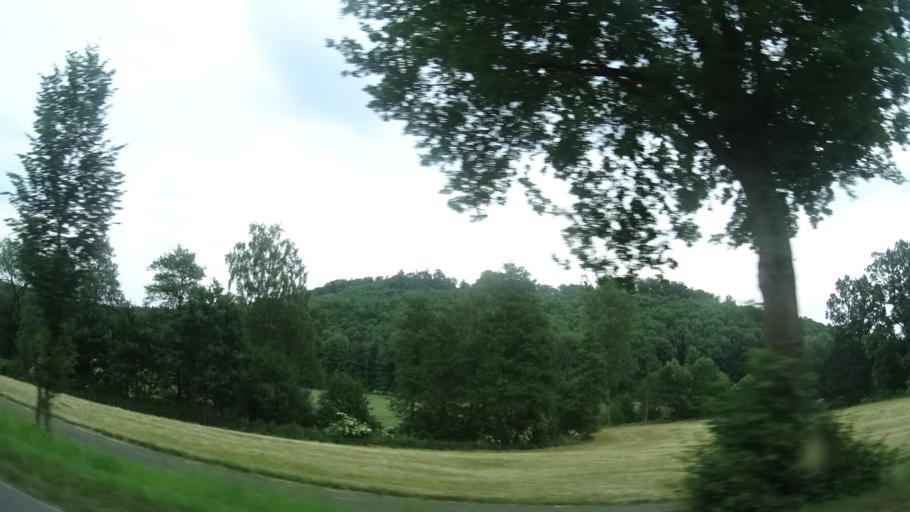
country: DE
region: North Rhine-Westphalia
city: Brakel
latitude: 51.7411
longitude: 9.1729
